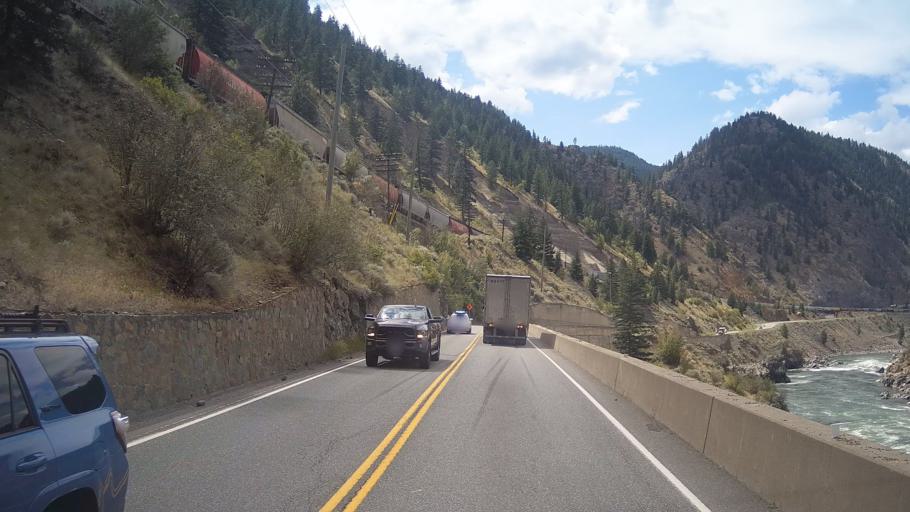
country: CA
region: British Columbia
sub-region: Thompson-Nicola Regional District
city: Ashcroft
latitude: 50.2578
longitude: -121.4338
